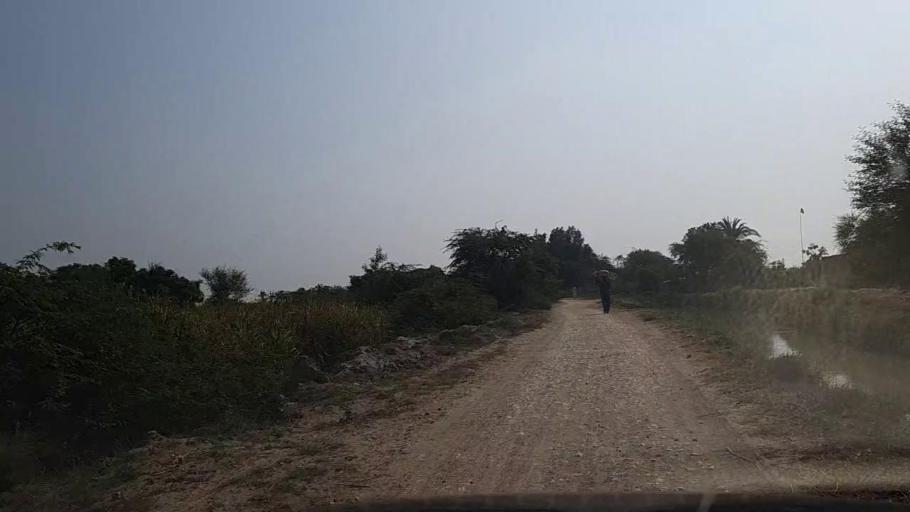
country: PK
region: Sindh
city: Mirpur Batoro
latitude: 24.7007
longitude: 68.2181
